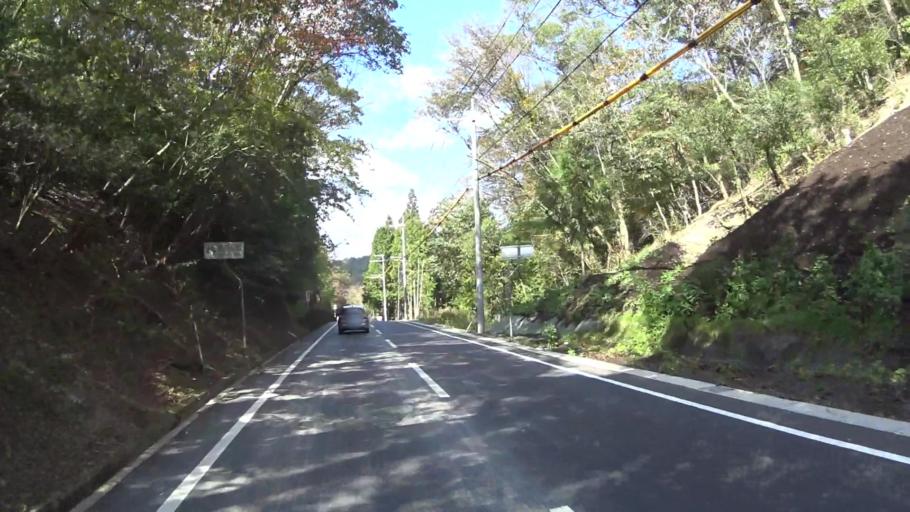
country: JP
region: Kyoto
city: Kameoka
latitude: 35.1640
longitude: 135.4587
